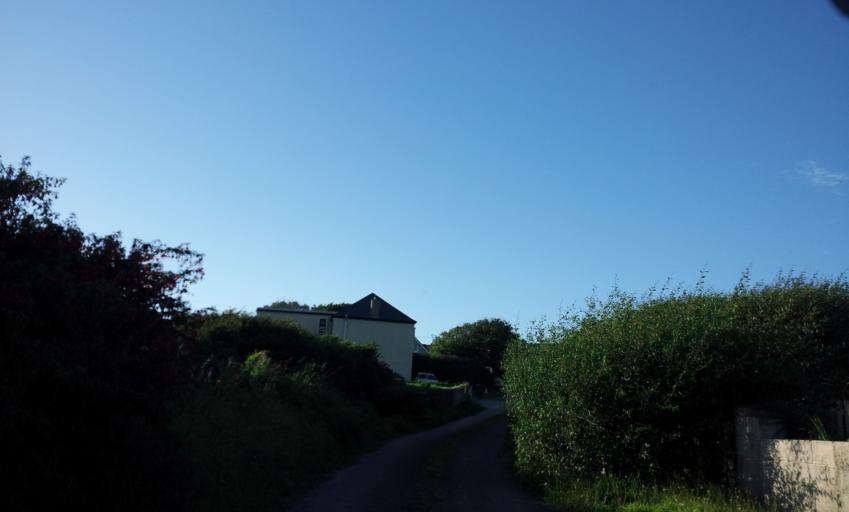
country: IE
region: Munster
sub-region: Ciarrai
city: Dingle
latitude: 52.1226
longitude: -10.3261
